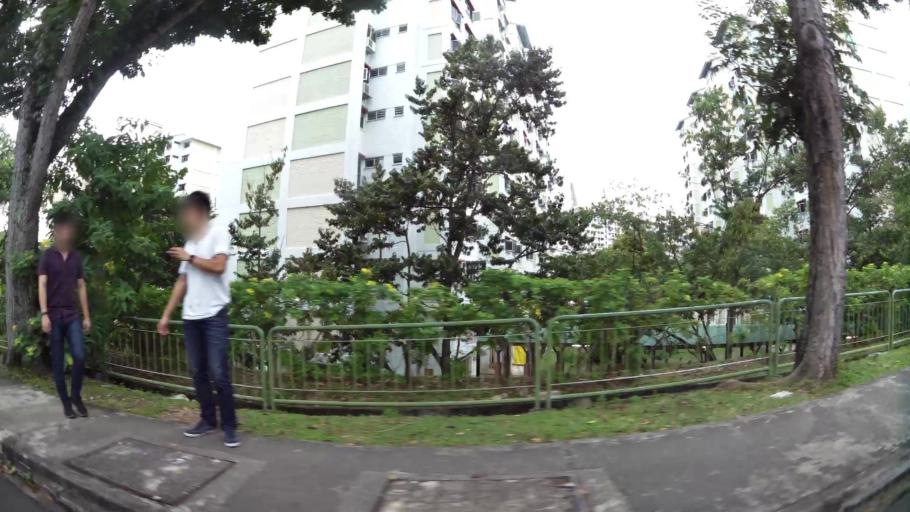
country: SG
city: Singapore
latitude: 1.3505
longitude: 103.8771
